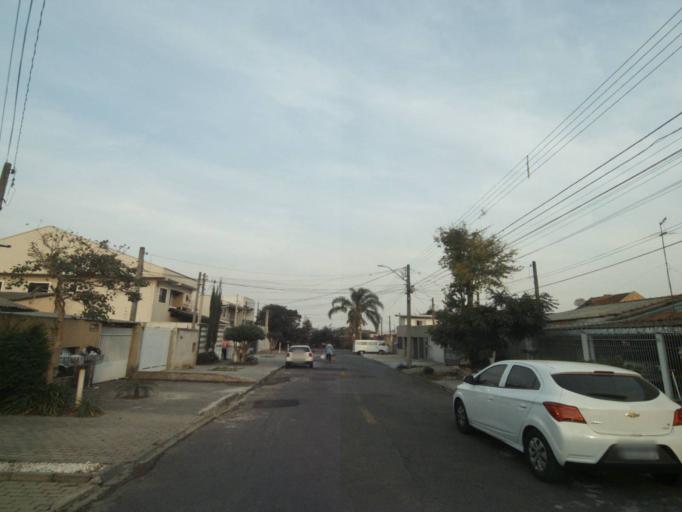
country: BR
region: Parana
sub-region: Pinhais
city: Pinhais
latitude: -25.4859
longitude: -49.2016
